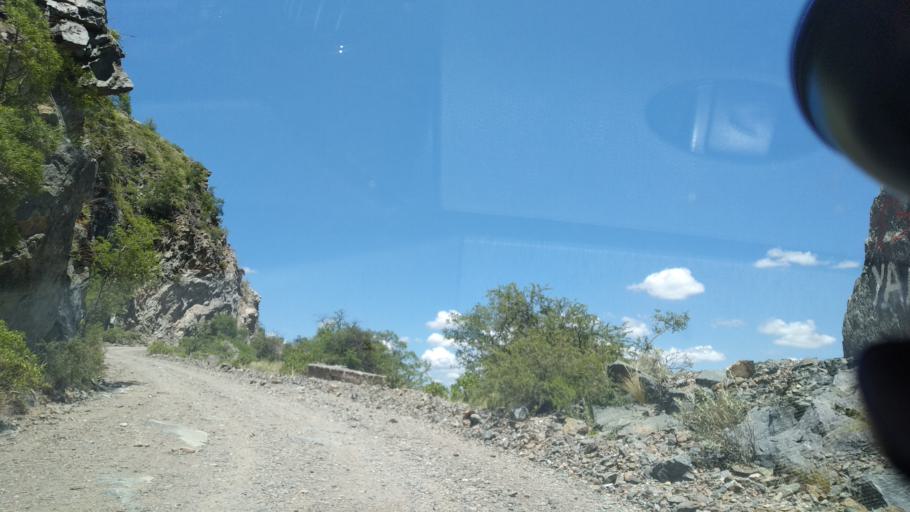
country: AR
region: Cordoba
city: Salsacate
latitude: -31.3721
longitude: -65.4065
